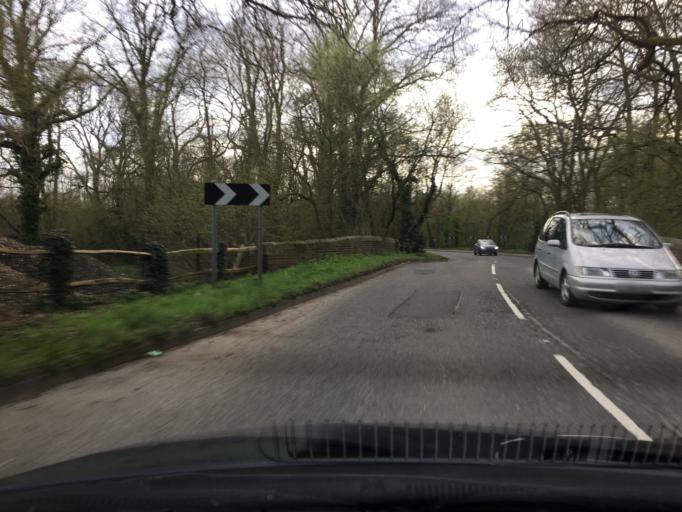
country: GB
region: England
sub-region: Hampshire
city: Yateley
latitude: 51.3465
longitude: -0.8154
